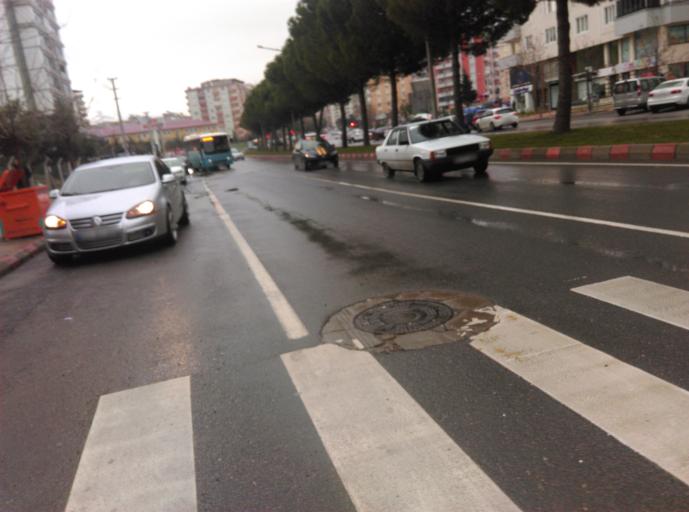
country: TR
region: Kahramanmaras
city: Kahramanmaras
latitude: 37.5839
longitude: 36.8884
